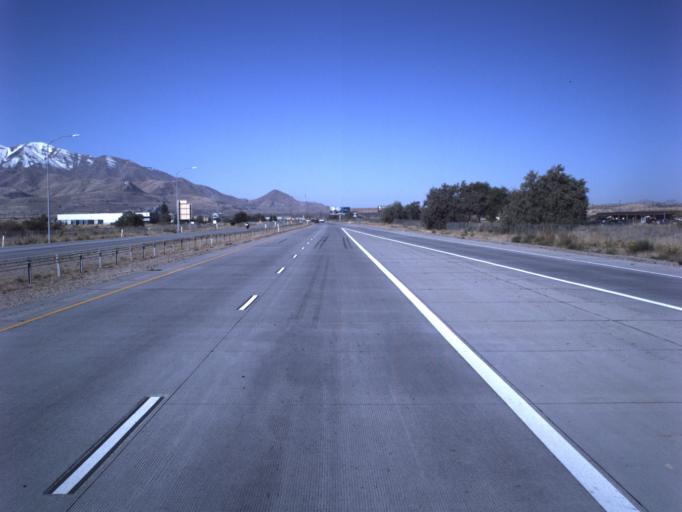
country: US
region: Utah
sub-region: Salt Lake County
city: West Valley City
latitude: 40.7259
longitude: -112.0294
